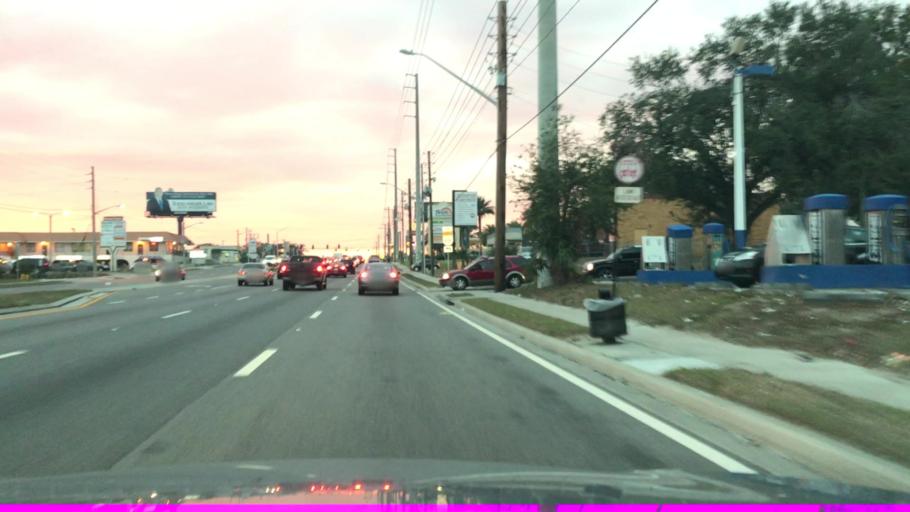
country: US
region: Florida
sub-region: Orange County
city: Pine Hills
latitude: 28.5778
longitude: -81.4731
